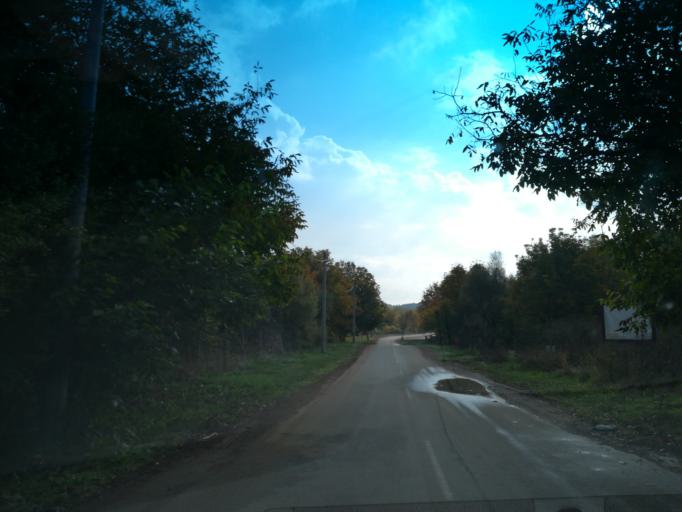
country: BG
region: Stara Zagora
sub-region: Obshtina Nikolaevo
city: Elkhovo
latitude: 42.3396
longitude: 25.4047
